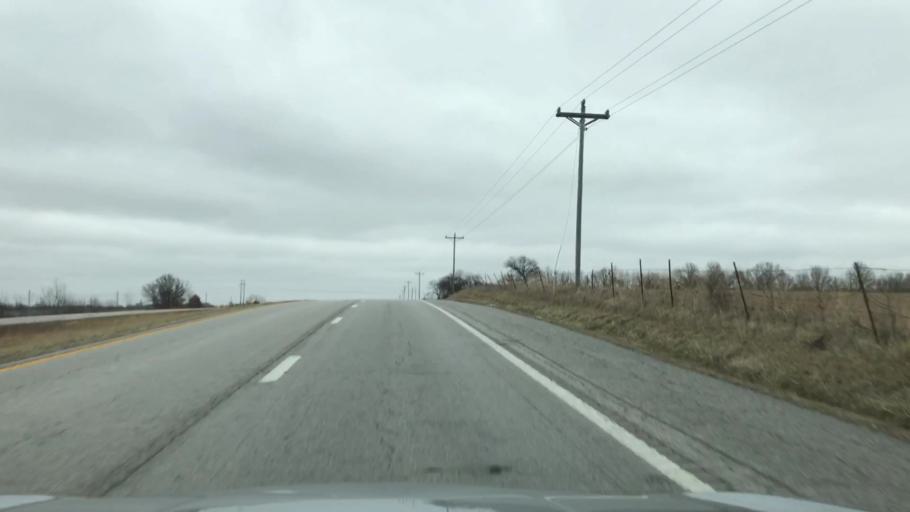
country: US
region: Missouri
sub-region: Linn County
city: Linneus
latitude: 39.7780
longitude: -93.2018
